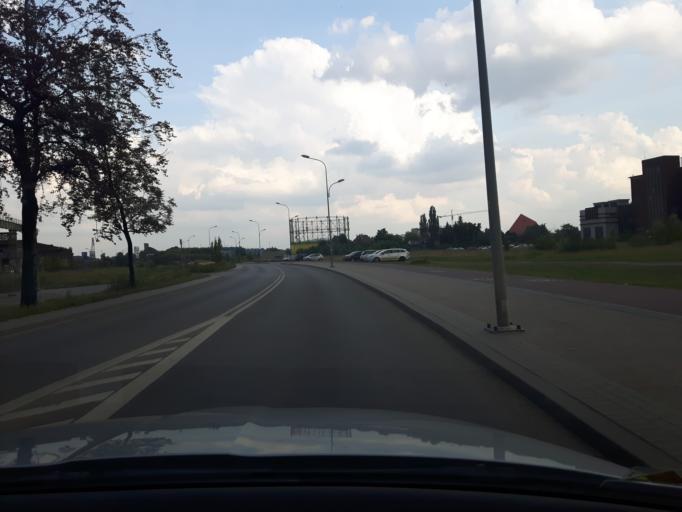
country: PL
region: Pomeranian Voivodeship
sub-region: Gdansk
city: Gdansk
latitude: 54.3613
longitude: 18.6535
